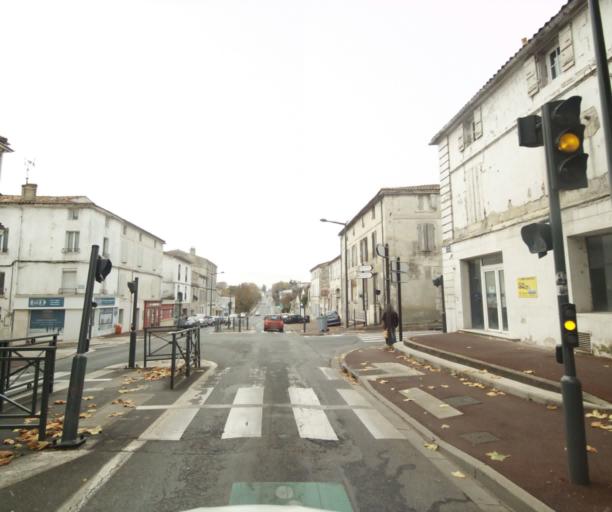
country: FR
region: Poitou-Charentes
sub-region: Departement de la Charente-Maritime
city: Saintes
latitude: 45.7433
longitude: -0.6400
